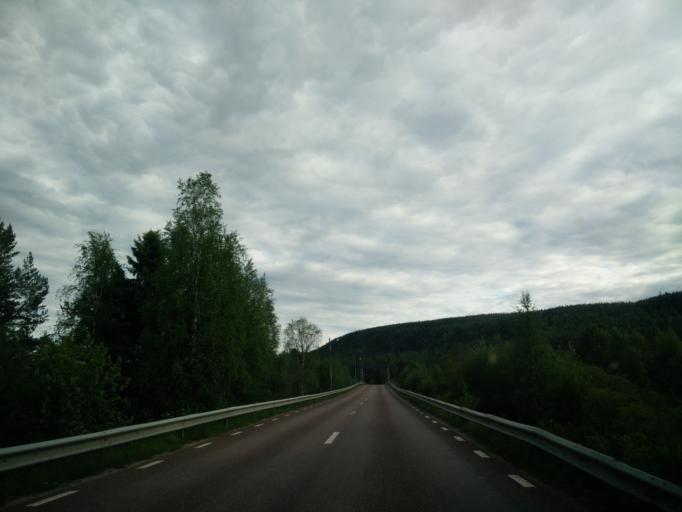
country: SE
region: Jaemtland
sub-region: Harjedalens Kommun
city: Sveg
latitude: 62.2757
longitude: 14.8057
